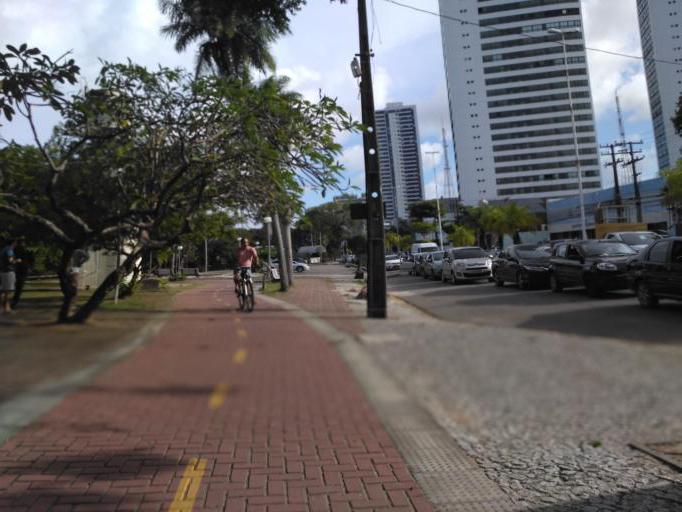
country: BR
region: Pernambuco
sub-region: Recife
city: Recife
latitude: -8.0505
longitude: -34.8740
